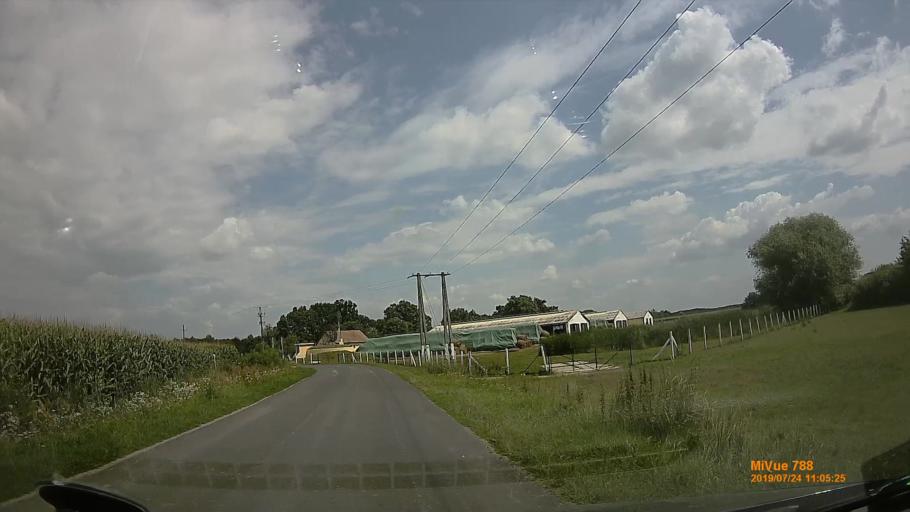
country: HU
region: Szabolcs-Szatmar-Bereg
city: Tarpa
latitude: 48.1794
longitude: 22.5183
